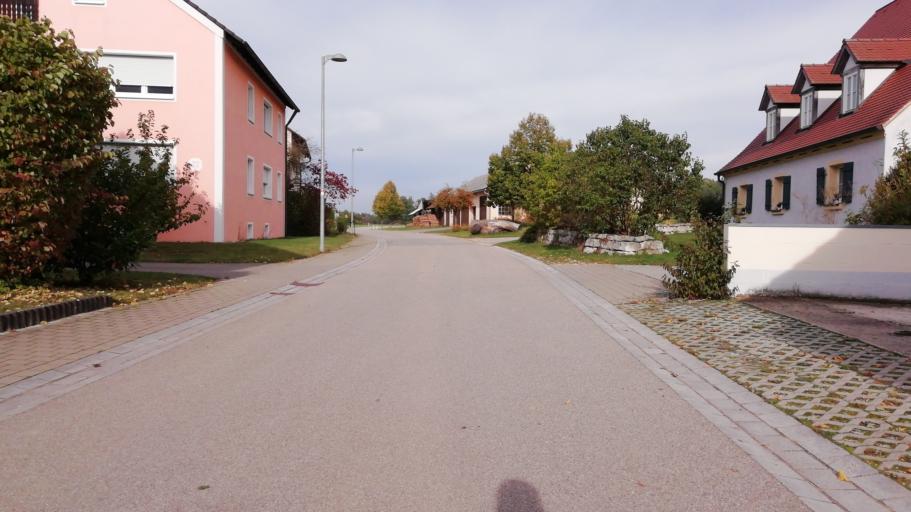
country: DE
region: Bavaria
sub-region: Regierungsbezirk Mittelfranken
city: Allersberg
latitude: 49.2636
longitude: 11.2156
